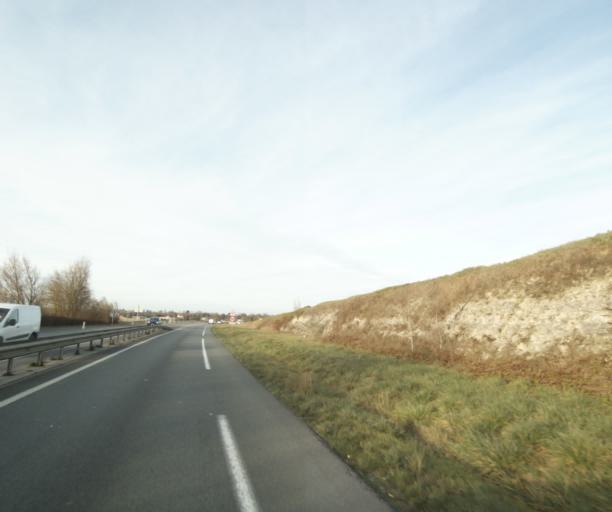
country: FR
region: Poitou-Charentes
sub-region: Departement de la Charente-Maritime
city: Saintes
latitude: 45.7306
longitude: -0.6577
